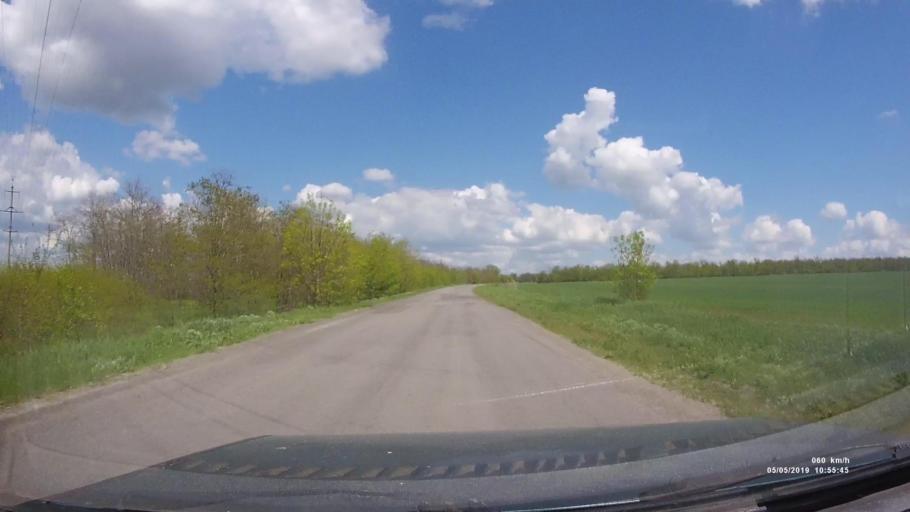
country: RU
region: Rostov
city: Ust'-Donetskiy
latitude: 47.6684
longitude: 40.8204
